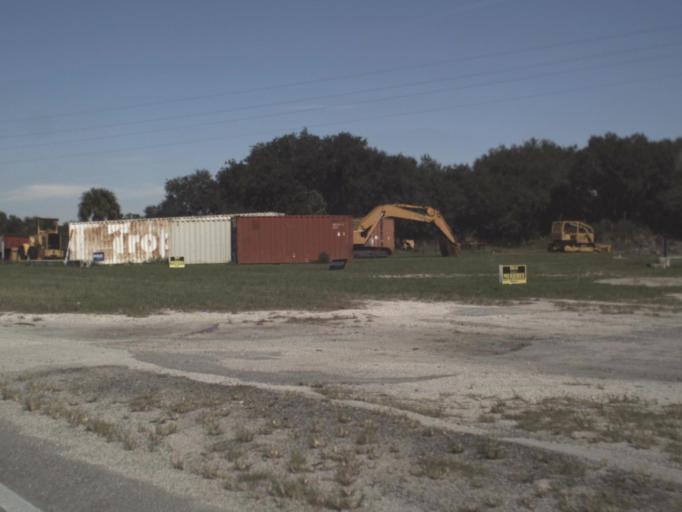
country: US
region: Florida
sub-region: Hendry County
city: Port LaBelle
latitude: 26.9456
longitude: -81.3164
